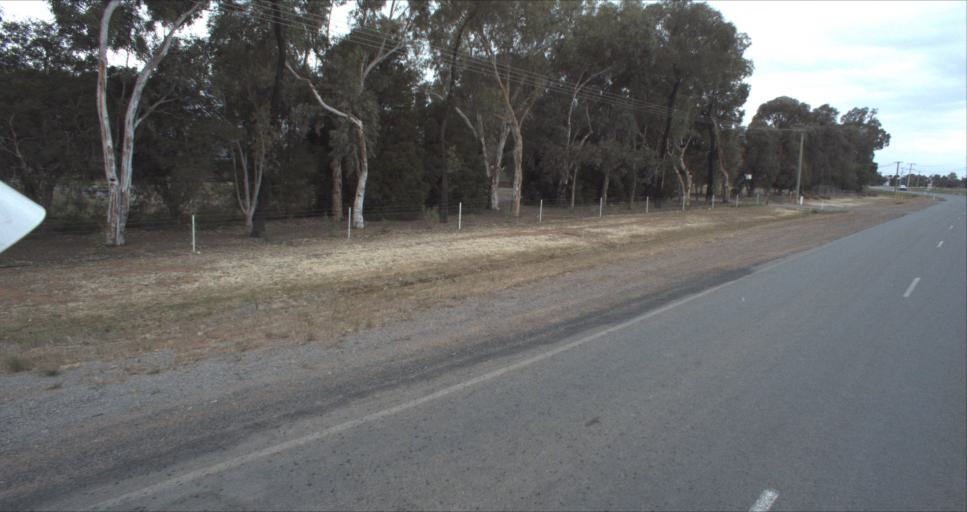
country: AU
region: New South Wales
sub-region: Leeton
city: Leeton
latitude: -34.5322
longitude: 146.3885
